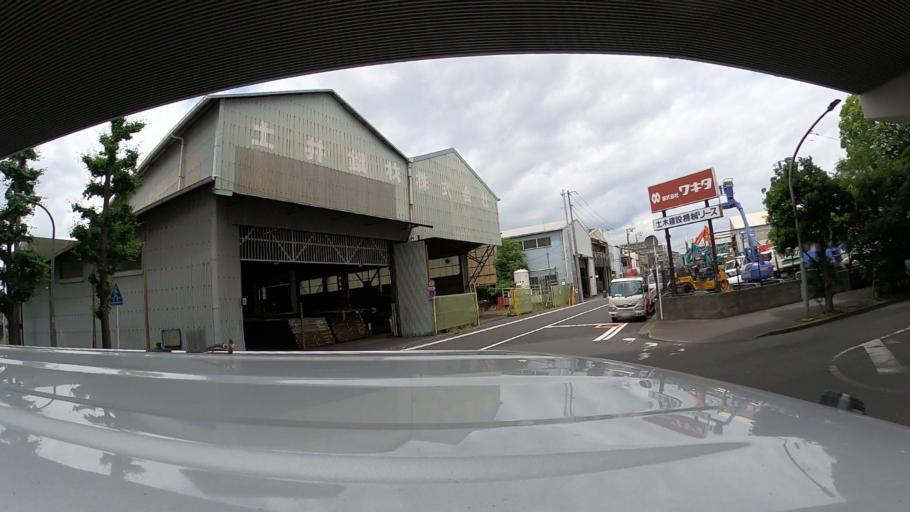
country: JP
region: Kanagawa
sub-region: Kawasaki-shi
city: Kawasaki
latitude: 35.5024
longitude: 139.6988
